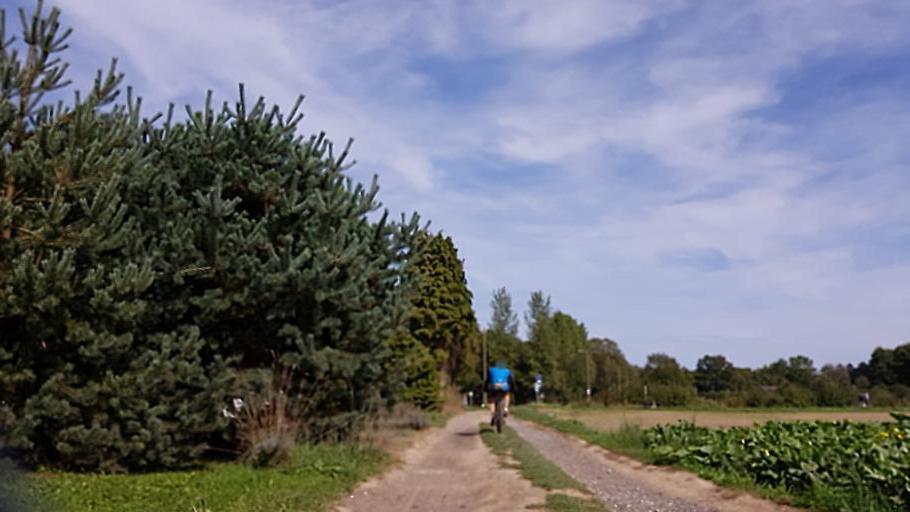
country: BE
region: Wallonia
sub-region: Province du Brabant Wallon
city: Beauvechain
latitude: 50.7771
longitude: 4.7301
